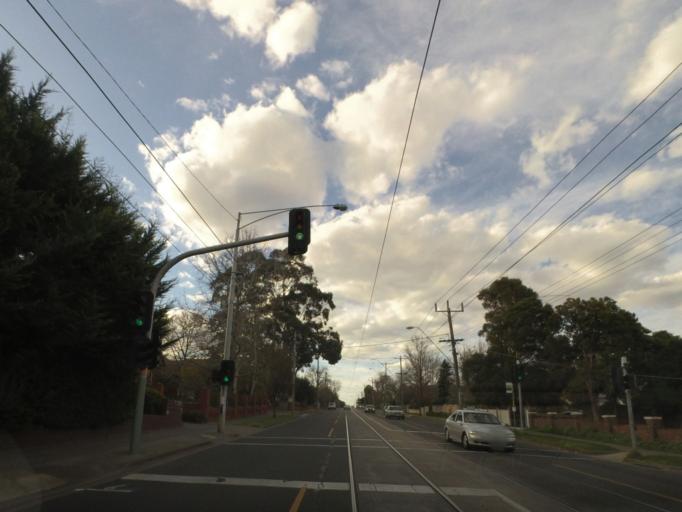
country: AU
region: Victoria
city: Glenferrie
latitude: -37.8403
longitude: 145.0549
